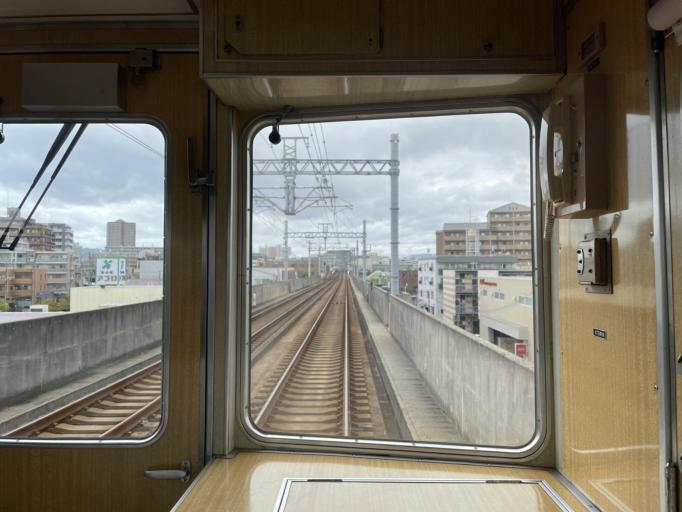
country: JP
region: Hyogo
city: Nishinomiya-hama
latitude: 34.7348
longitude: 135.3533
